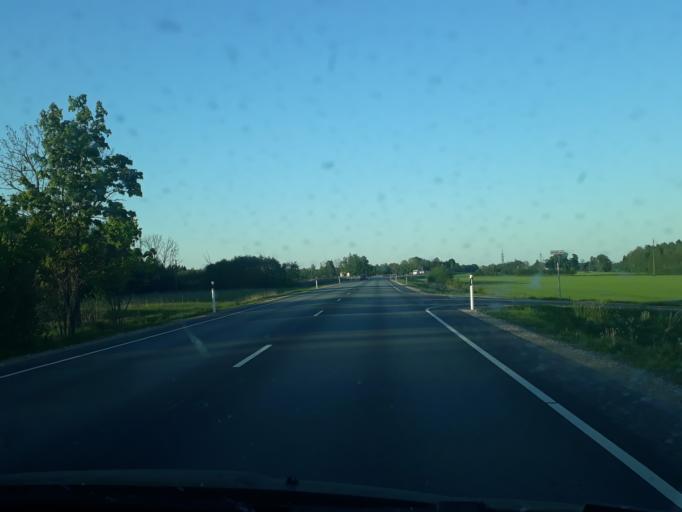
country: EE
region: Paernumaa
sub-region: Tootsi vald
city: Tootsi
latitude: 58.4976
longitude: 24.7736
